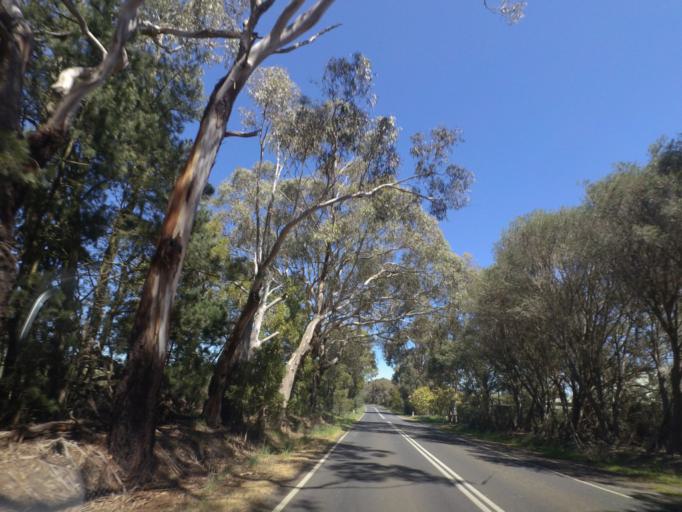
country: AU
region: Victoria
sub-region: Hume
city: Sunbury
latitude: -37.2929
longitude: 144.6979
